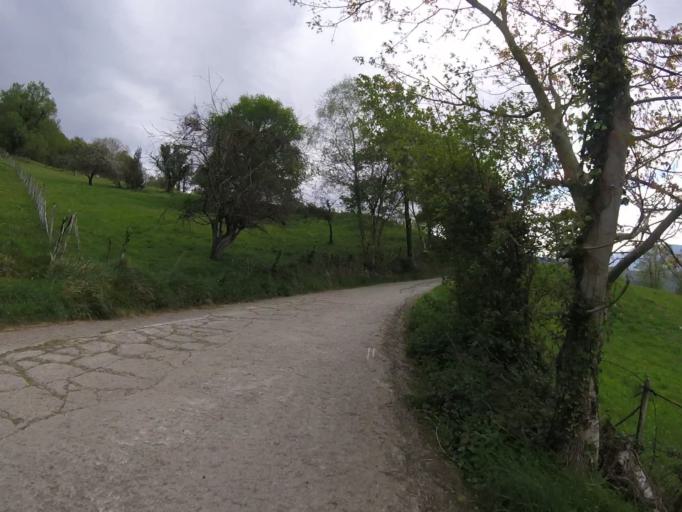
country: ES
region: Basque Country
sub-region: Provincia de Guipuzcoa
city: Aizarnazabal
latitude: 43.2531
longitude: -2.2091
